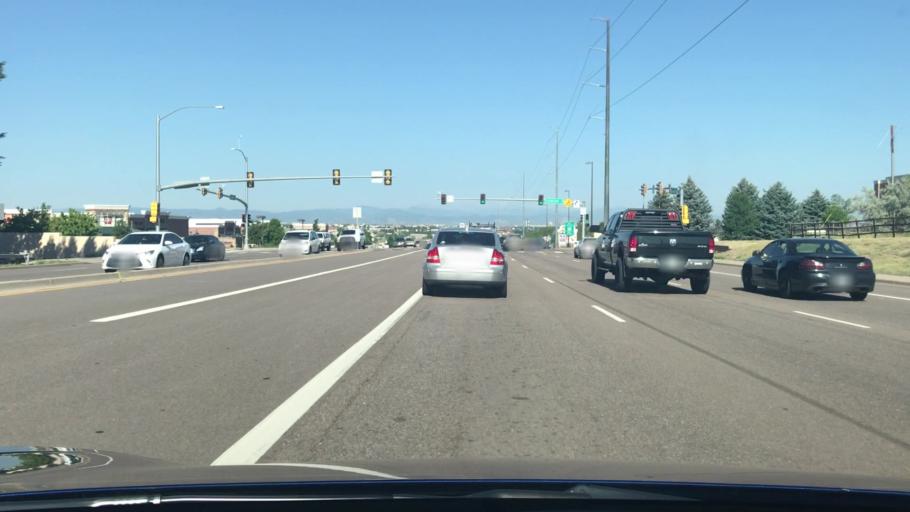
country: US
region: Colorado
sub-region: Arapahoe County
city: Dove Valley
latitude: 39.5950
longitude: -104.7957
